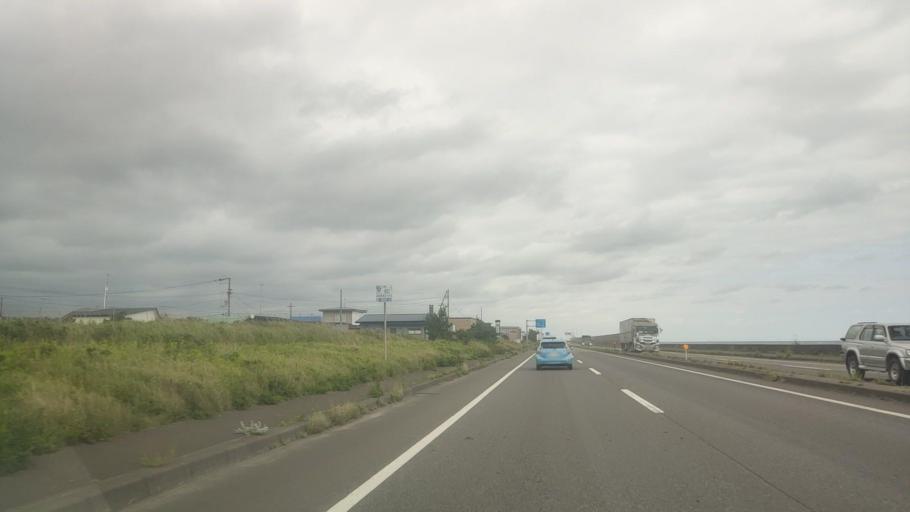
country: JP
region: Hokkaido
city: Shiraoi
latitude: 42.5474
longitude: 141.3597
